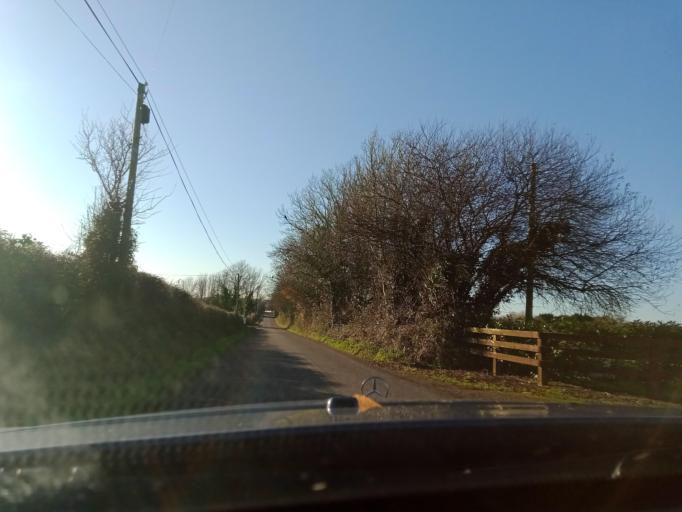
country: IE
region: Leinster
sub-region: Kilkenny
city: Mooncoin
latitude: 52.2969
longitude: -7.2225
